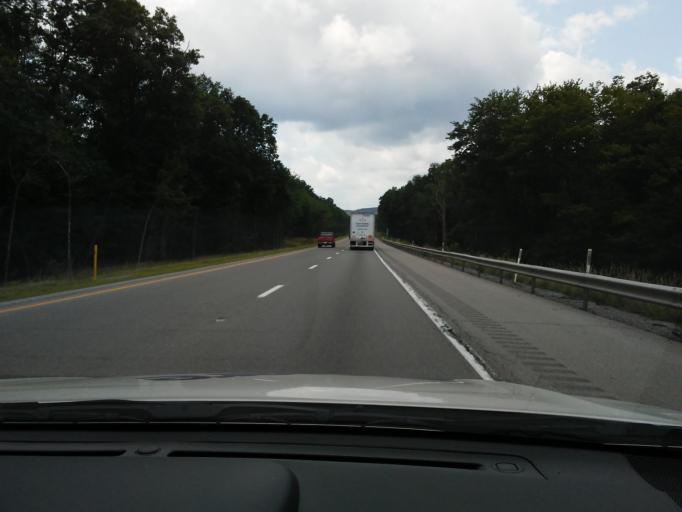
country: US
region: Pennsylvania
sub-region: Centre County
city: Stormstown
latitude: 40.9944
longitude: -78.0096
